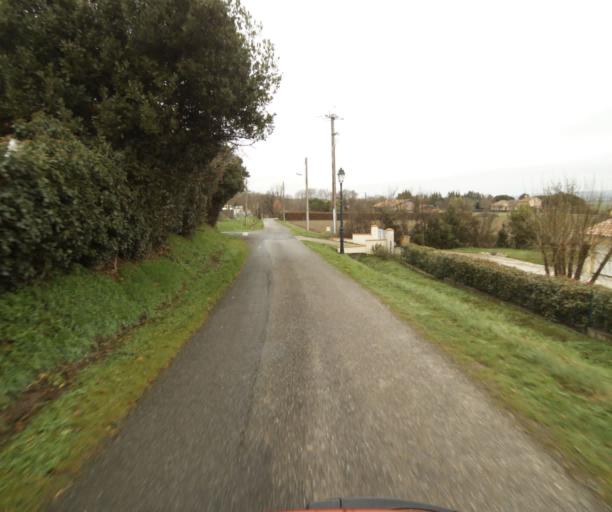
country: FR
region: Midi-Pyrenees
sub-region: Departement de la Haute-Garonne
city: Gaillac-Toulza
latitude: 43.2622
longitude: 1.5164
